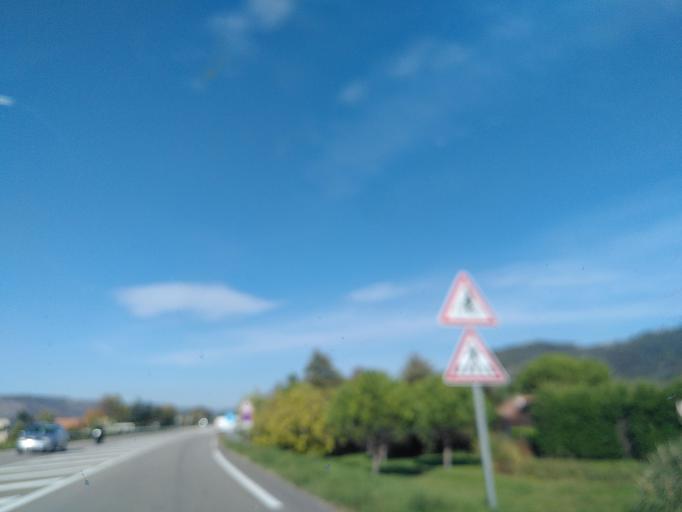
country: FR
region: Rhone-Alpes
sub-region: Departement de la Drome
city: Saint-Vallier
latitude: 45.1714
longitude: 4.8145
